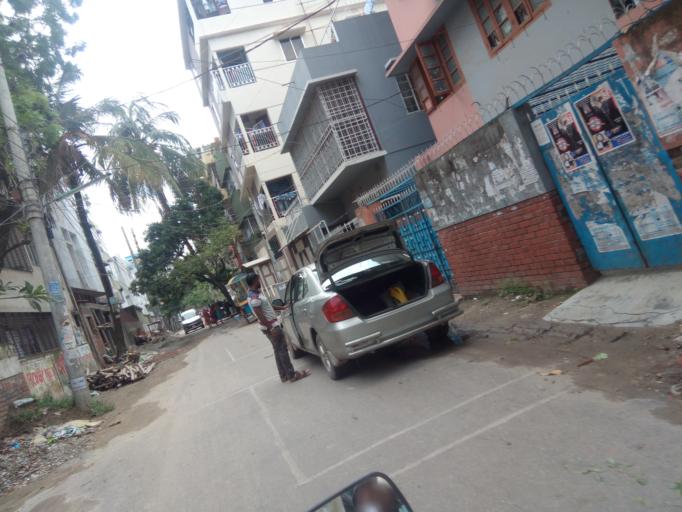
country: BD
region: Dhaka
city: Azimpur
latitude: 23.7666
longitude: 90.3636
